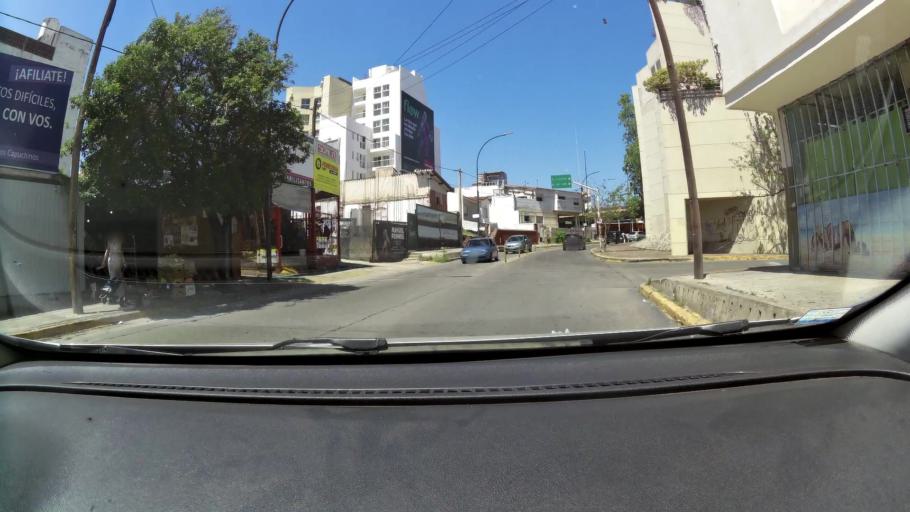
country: AR
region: Cordoba
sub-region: Departamento de Capital
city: Cordoba
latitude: -31.4134
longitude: -64.2018
